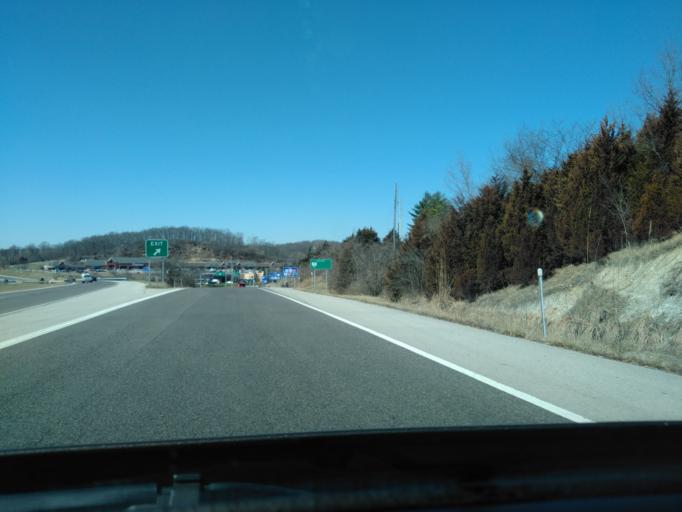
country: US
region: Missouri
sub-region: Saint Louis County
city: Fenton
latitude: 38.5155
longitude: -90.4431
